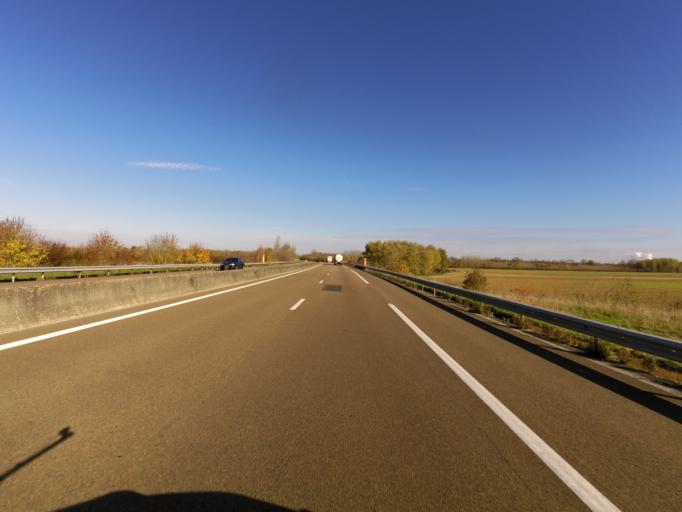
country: FR
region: Champagne-Ardenne
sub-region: Departement de la Marne
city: Fagnieres
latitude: 48.9863
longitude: 4.2935
